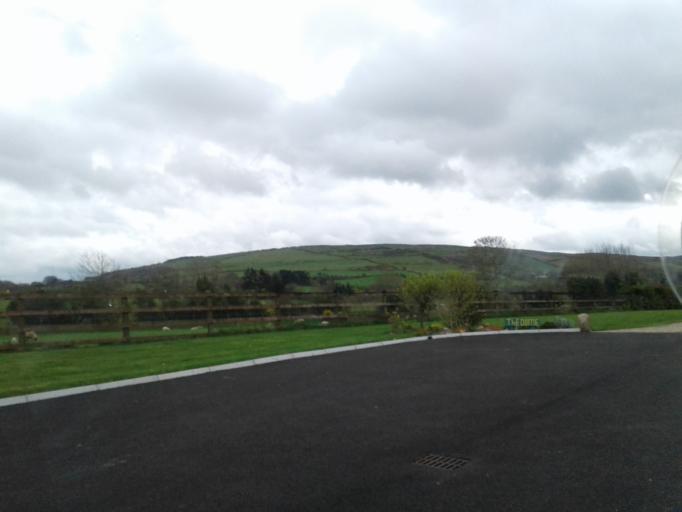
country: IE
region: Leinster
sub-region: Wicklow
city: Rathdrum
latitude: 53.0565
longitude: -6.2430
